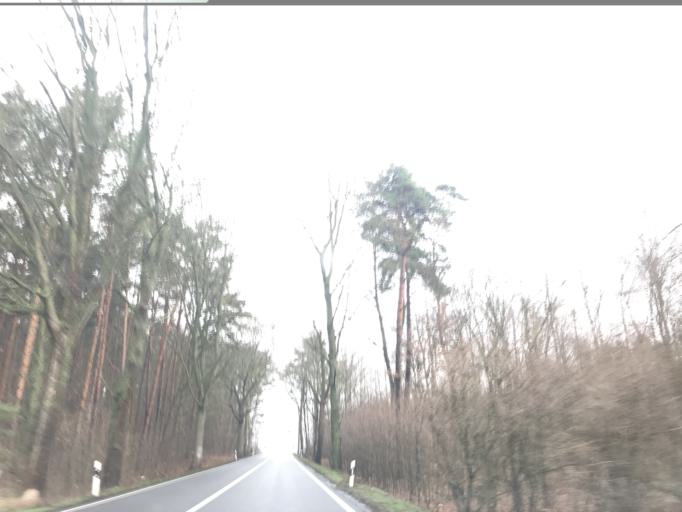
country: DE
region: Brandenburg
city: Kremmen
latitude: 52.7117
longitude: 12.9745
